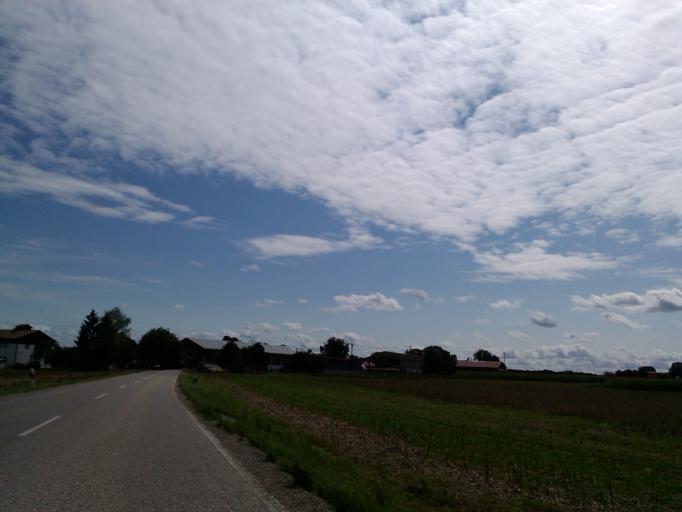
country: DE
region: Bavaria
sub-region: Upper Bavaria
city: Gilching
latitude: 48.0703
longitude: 11.3213
